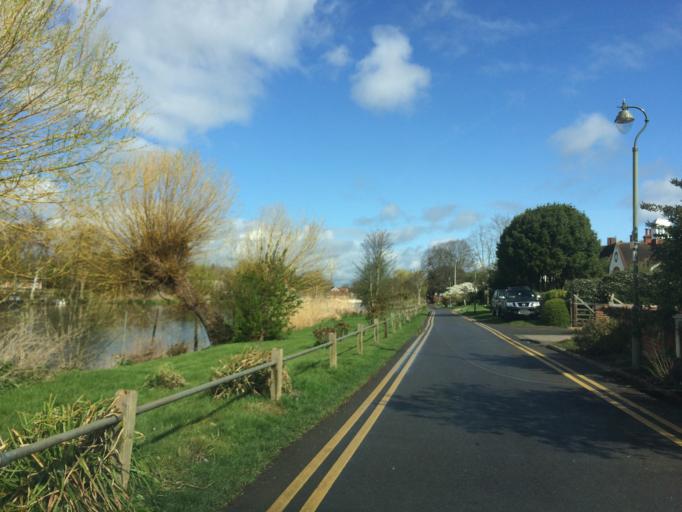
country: GB
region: England
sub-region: Surrey
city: Chertsey
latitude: 51.4068
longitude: -0.4925
